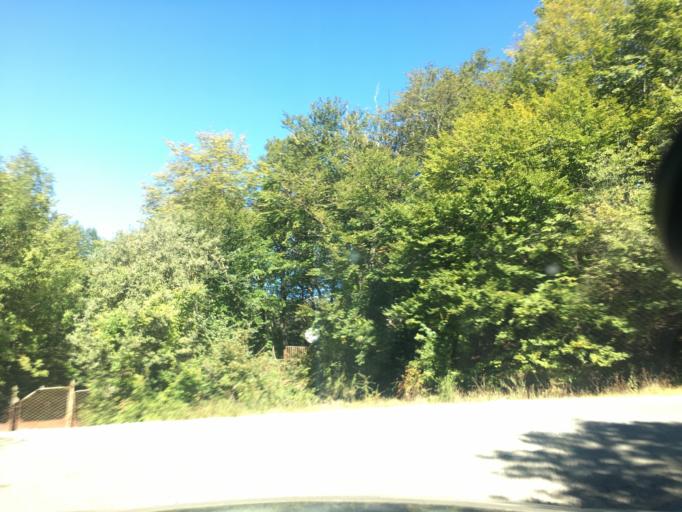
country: GE
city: Didi Lilo
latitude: 41.8848
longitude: 44.9176
